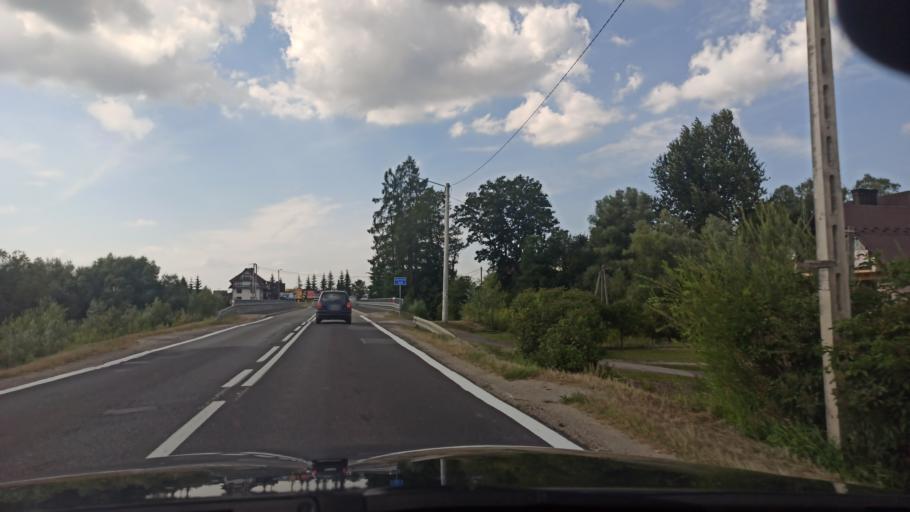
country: PL
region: Lesser Poland Voivodeship
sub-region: Powiat nowotarski
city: Ostrowsko
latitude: 49.4731
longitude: 20.1122
